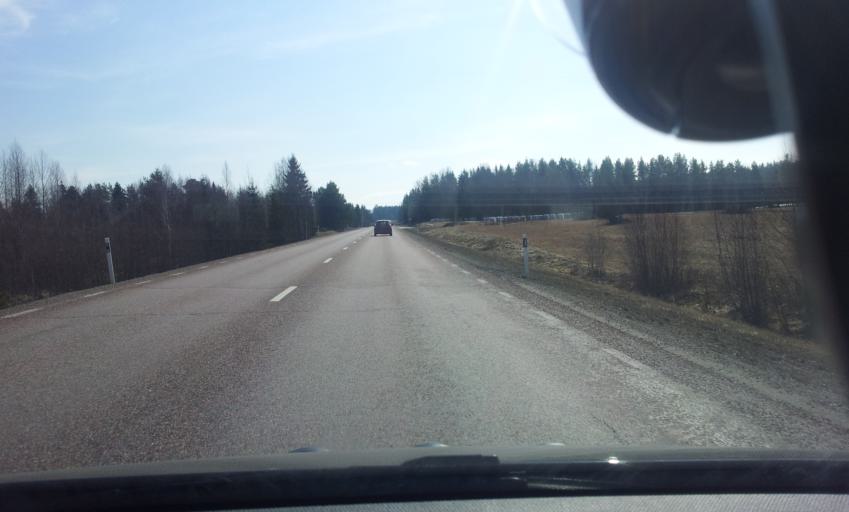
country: SE
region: Gaevleborg
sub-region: Ljusdals Kommun
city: Jaervsoe
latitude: 61.7800
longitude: 16.1424
